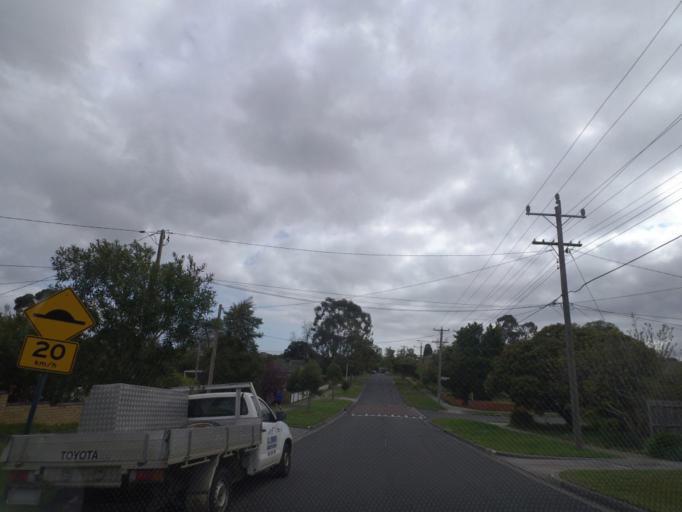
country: AU
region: Victoria
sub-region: Whitehorse
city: Nunawading
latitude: -37.8118
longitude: 145.1850
